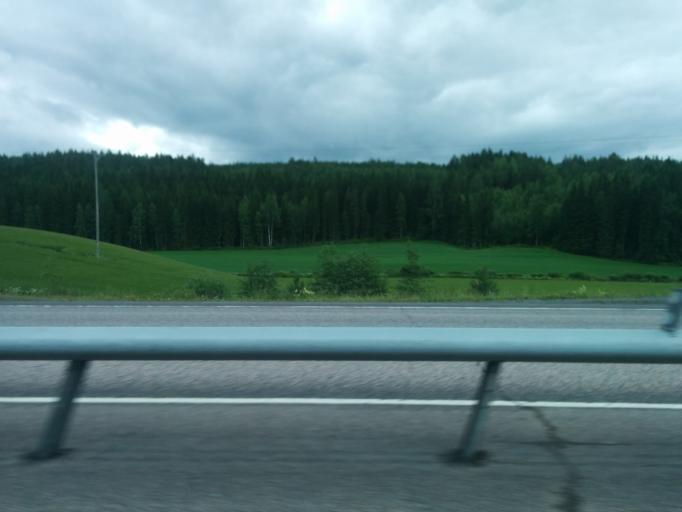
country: FI
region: Pirkanmaa
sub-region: Tampere
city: Orivesi
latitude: 61.6967
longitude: 24.4217
